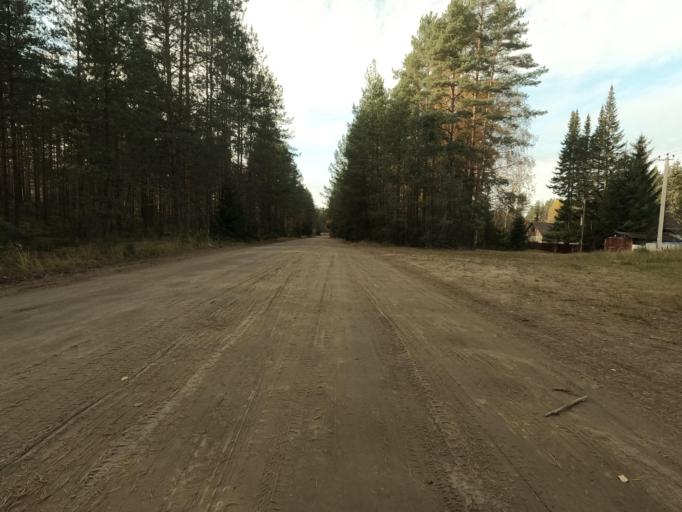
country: RU
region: Leningrad
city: Priladozhskiy
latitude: 59.6308
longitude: 31.3935
